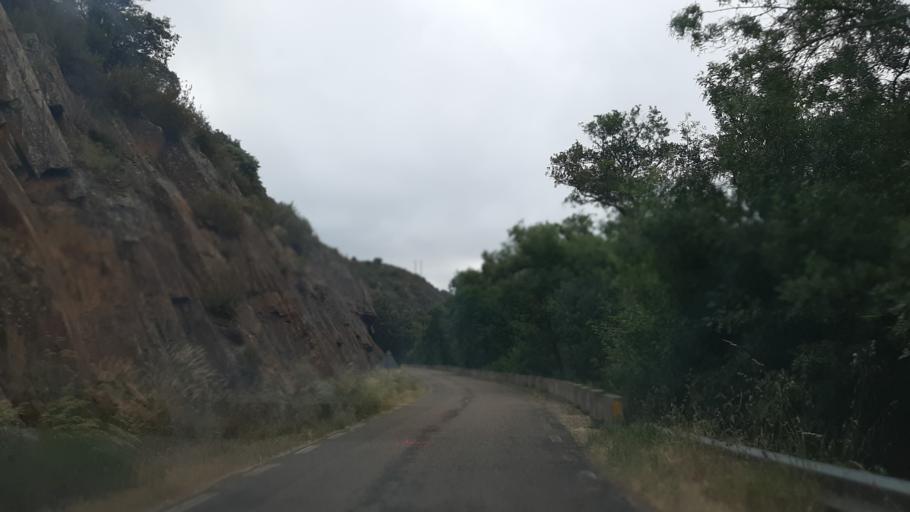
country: ES
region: Castille and Leon
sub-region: Provincia de Salamanca
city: Pastores
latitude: 40.5423
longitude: -6.4887
